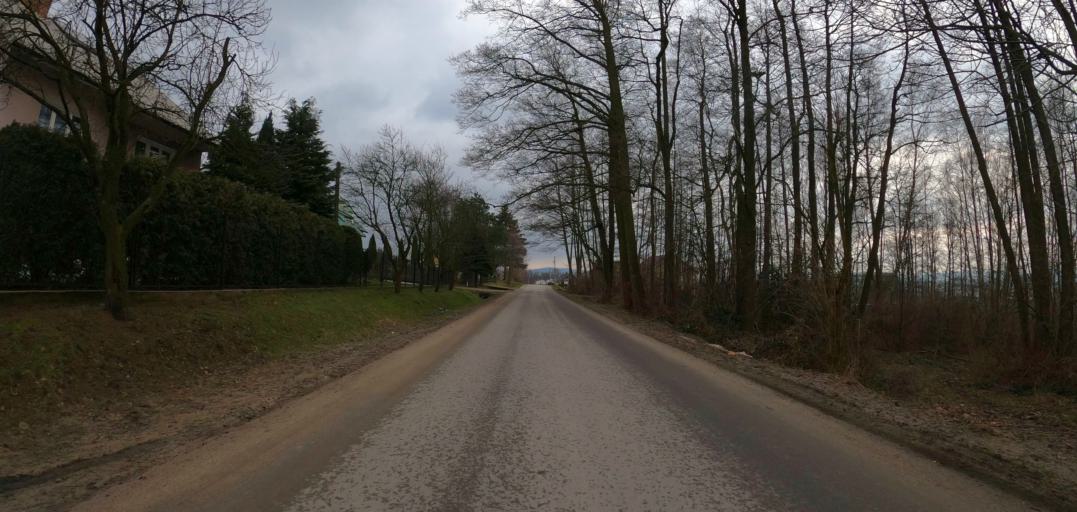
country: PL
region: Subcarpathian Voivodeship
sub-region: Powiat debicki
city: Pilzno
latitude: 49.9923
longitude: 21.3224
